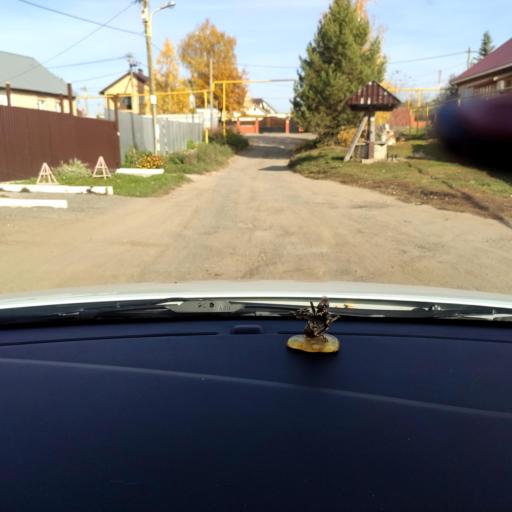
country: RU
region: Tatarstan
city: Vysokaya Gora
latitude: 55.7973
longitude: 49.2691
